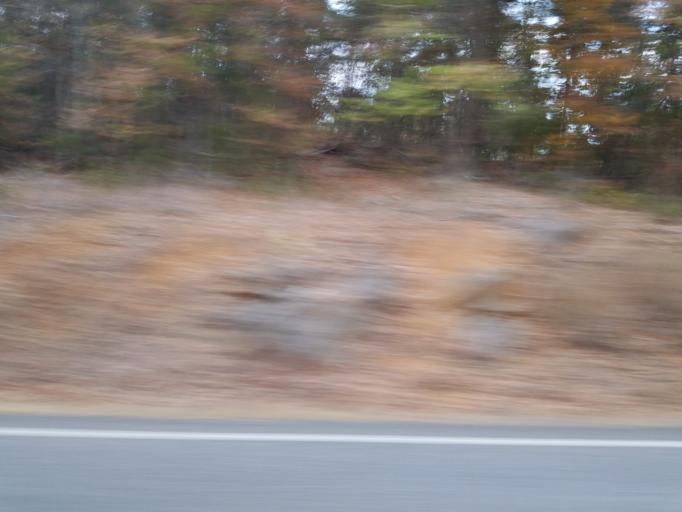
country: US
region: Georgia
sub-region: Murray County
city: Chatsworth
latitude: 34.5893
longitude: -84.6815
